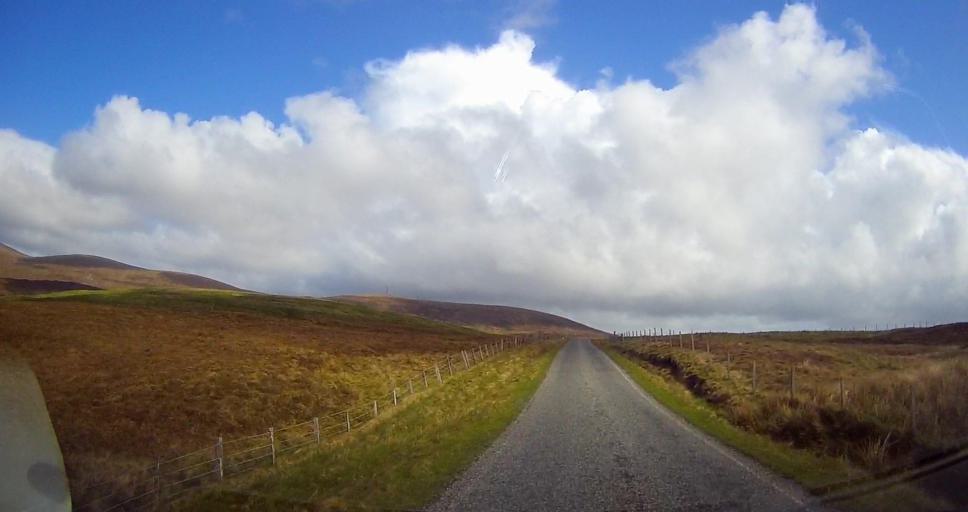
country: GB
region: Scotland
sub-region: Shetland Islands
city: Lerwick
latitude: 60.5105
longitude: -1.3862
